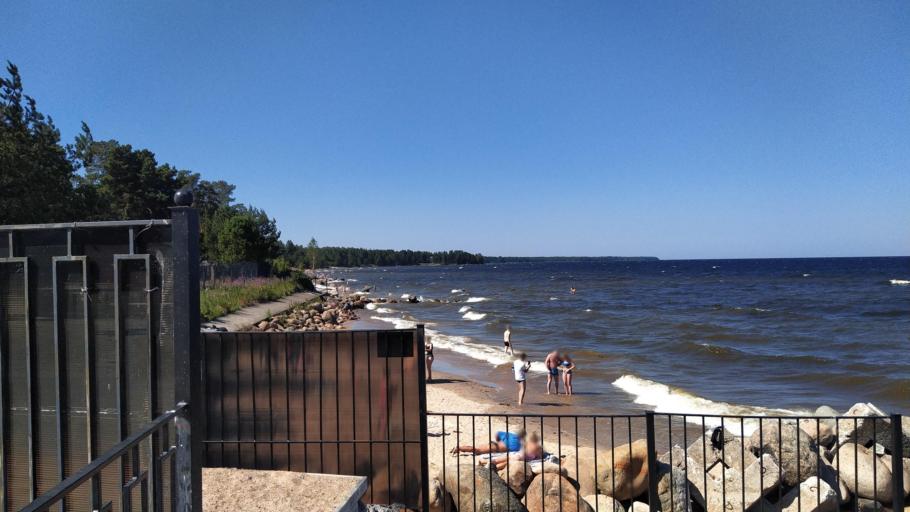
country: RU
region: Leningrad
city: Borisova Griva
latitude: 60.1249
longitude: 31.0760
